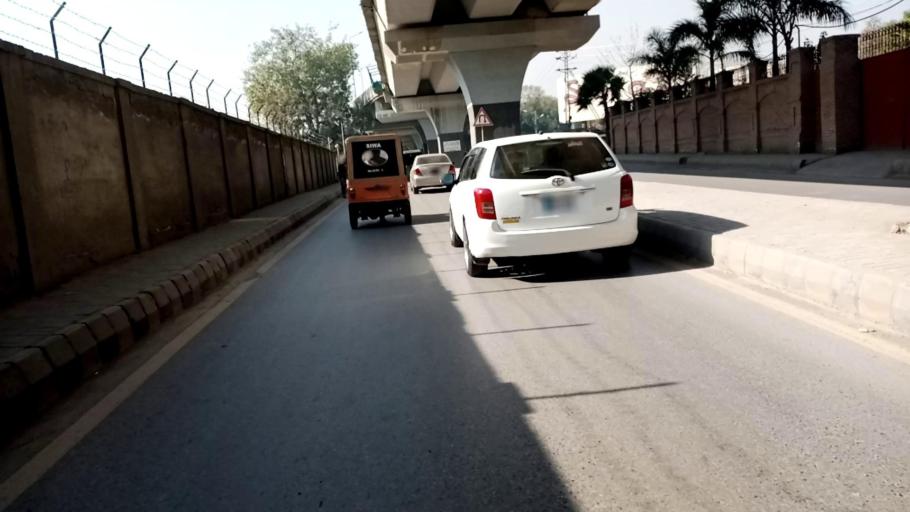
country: PK
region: Khyber Pakhtunkhwa
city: Peshawar
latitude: 34.0034
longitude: 71.5511
